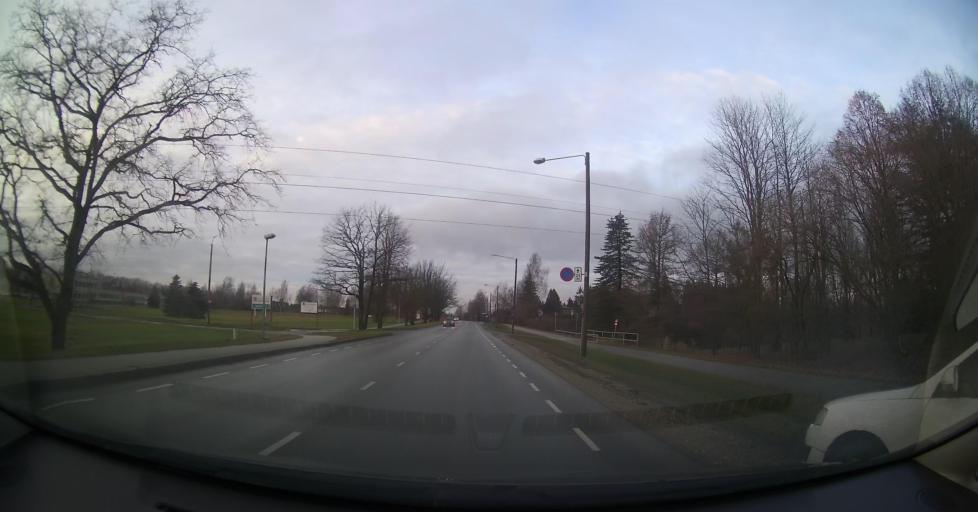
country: EE
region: Tartu
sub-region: Tartu linn
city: Tartu
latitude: 58.3920
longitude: 26.6923
